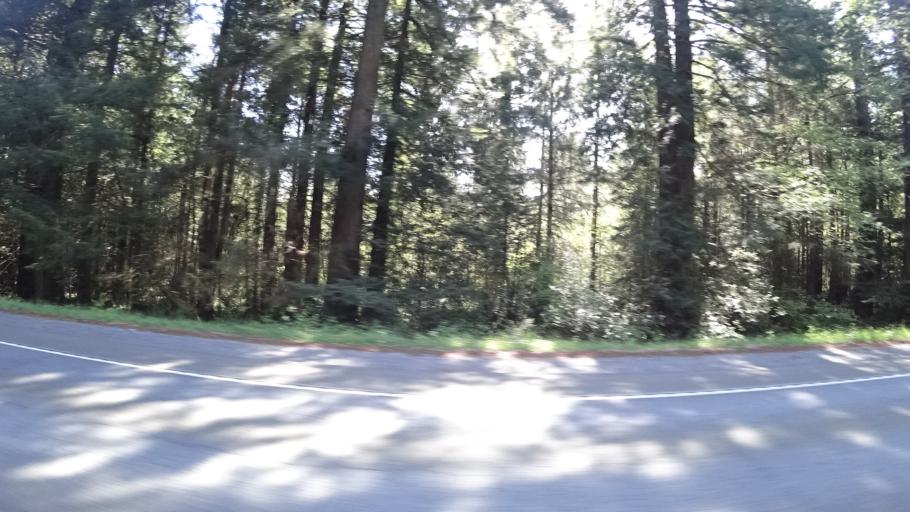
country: US
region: California
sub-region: Del Norte County
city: Bertsch-Oceanview
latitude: 41.8156
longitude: -124.1464
